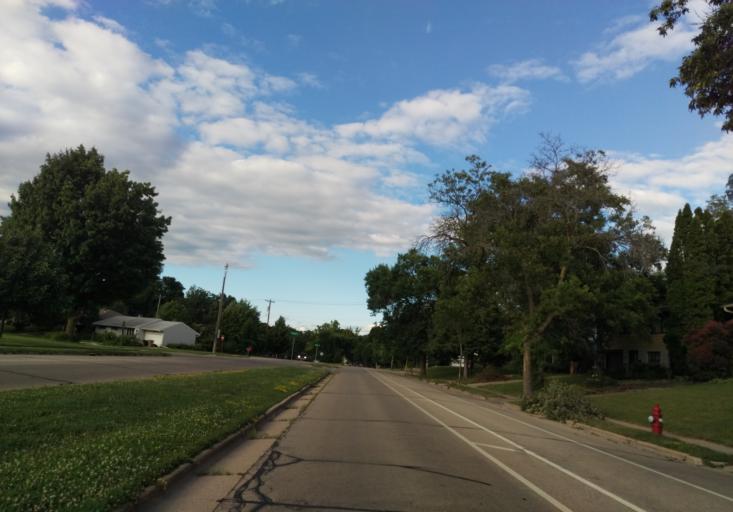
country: US
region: Wisconsin
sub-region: Dane County
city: Shorewood Hills
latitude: 43.0560
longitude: -89.4615
